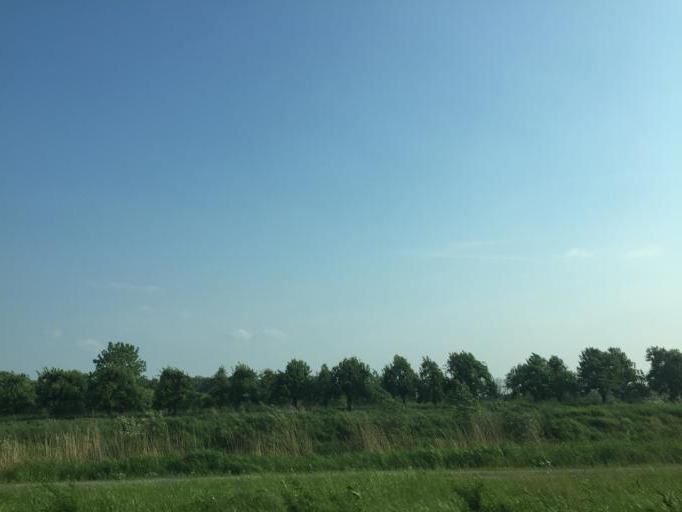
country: DE
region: Hamburg
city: Altona
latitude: 53.5128
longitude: 9.8726
